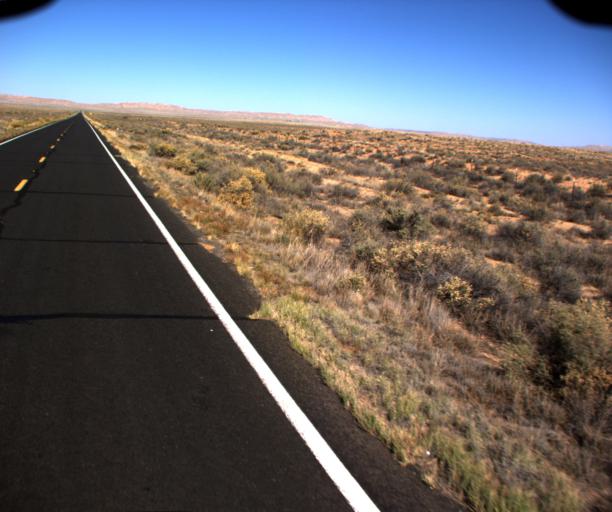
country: US
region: Arizona
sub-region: Navajo County
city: First Mesa
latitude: 35.6838
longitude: -110.5015
